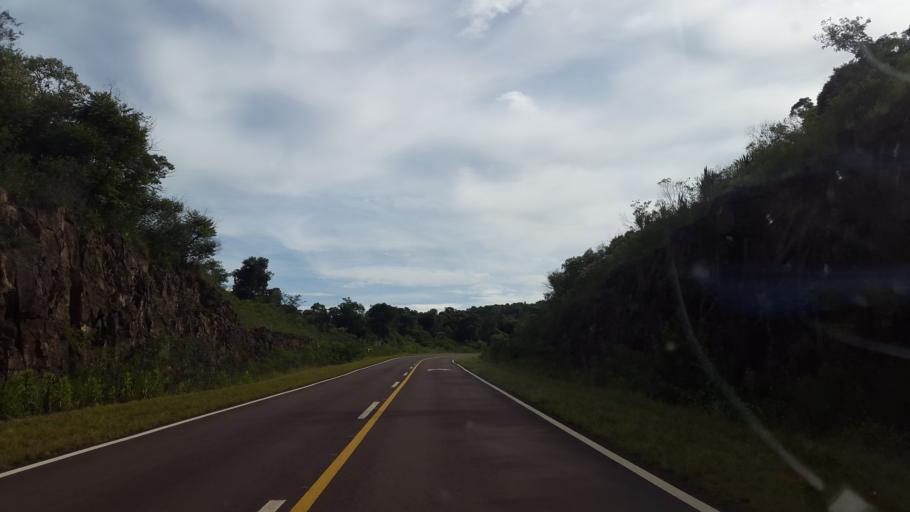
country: AR
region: Misiones
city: Bernardo de Irigoyen
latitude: -26.3228
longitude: -53.7552
